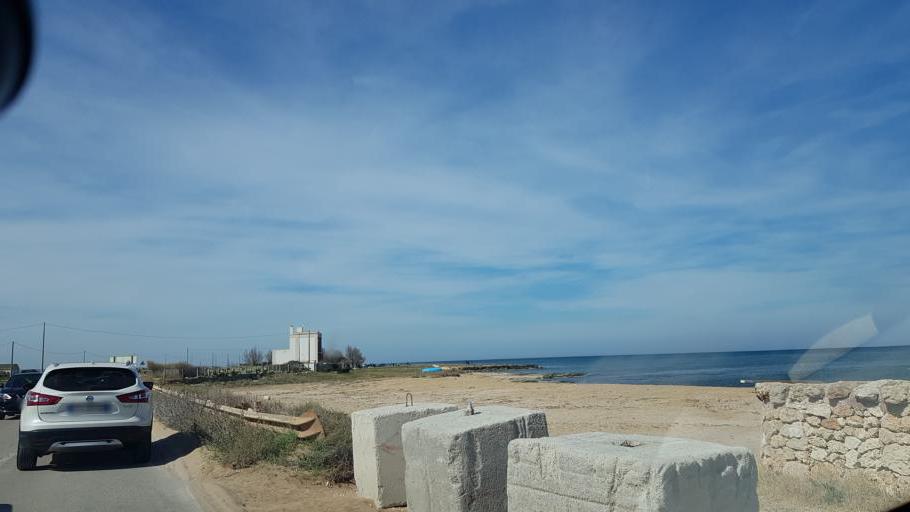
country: IT
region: Apulia
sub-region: Provincia di Brindisi
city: Pezze di Greco
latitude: 40.8539
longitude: 17.4437
